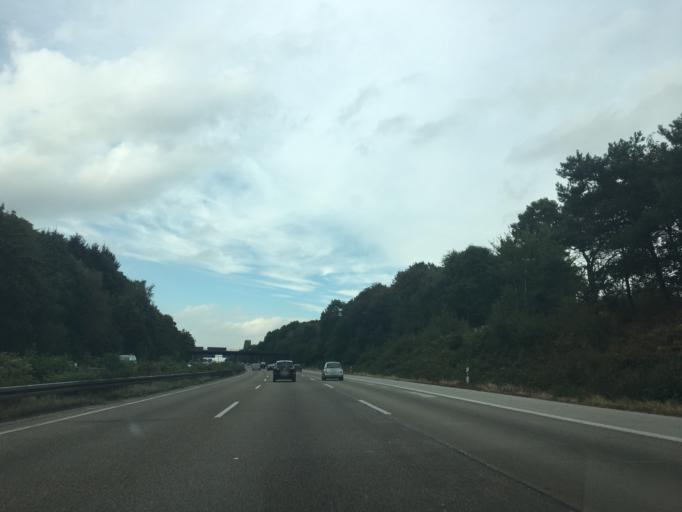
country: DE
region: North Rhine-Westphalia
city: Leichlingen
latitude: 51.1160
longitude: 6.9856
